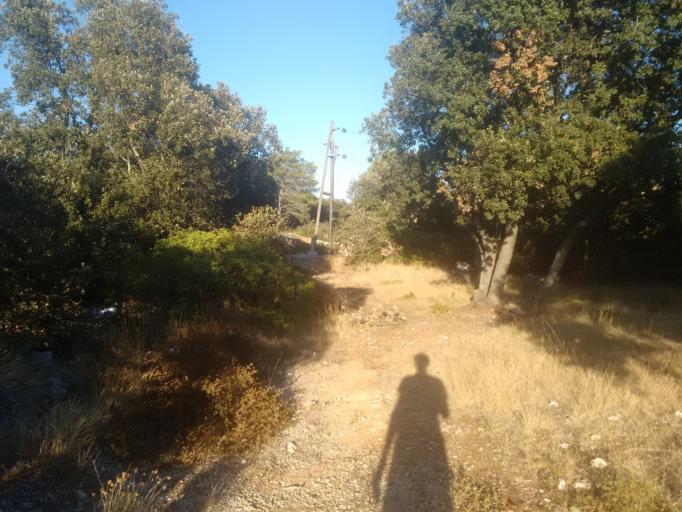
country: HR
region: Licko-Senjska
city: Novalja
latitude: 44.3698
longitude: 14.7007
